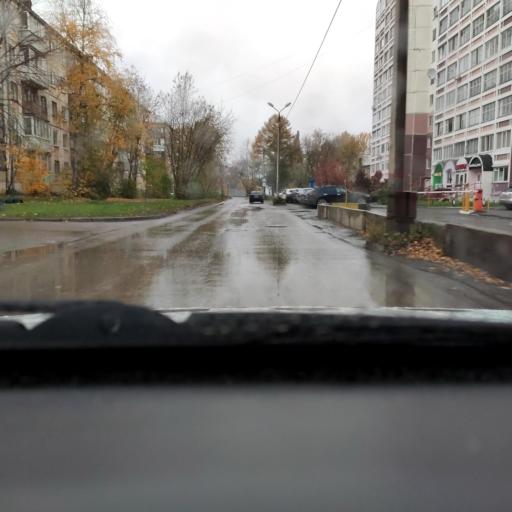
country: RU
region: Perm
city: Perm
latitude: 58.0040
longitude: 56.2943
